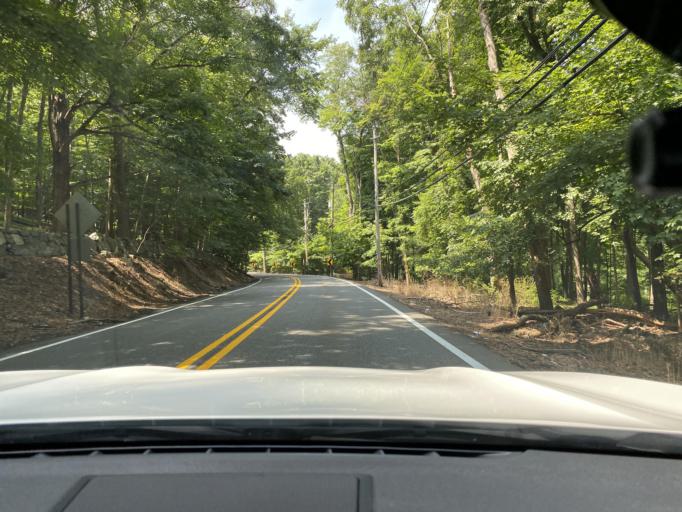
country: US
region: New Jersey
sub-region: Bergen County
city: Mahwah
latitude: 41.0770
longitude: -74.1930
